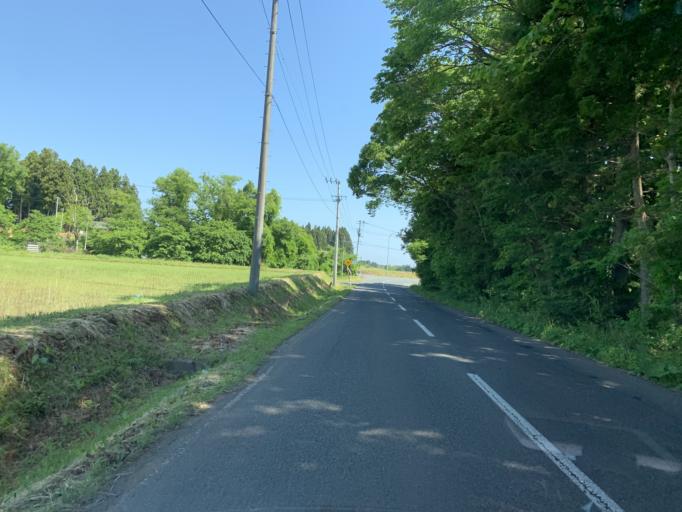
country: JP
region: Iwate
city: Mizusawa
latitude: 39.0767
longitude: 141.0620
